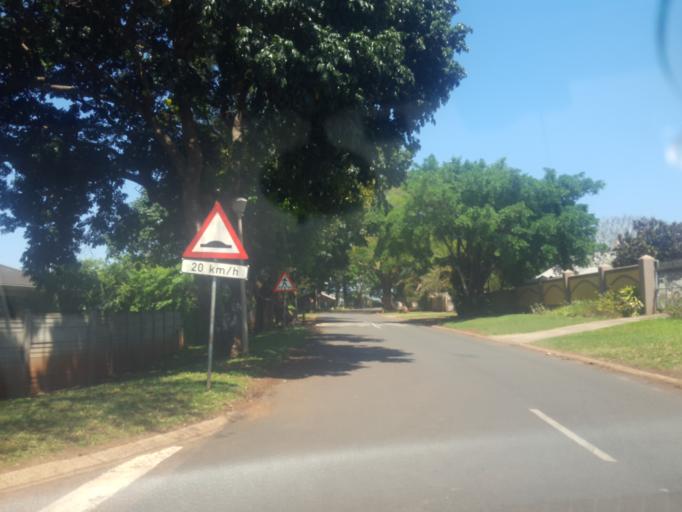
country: ZA
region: KwaZulu-Natal
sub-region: uThungulu District Municipality
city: Empangeni
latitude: -28.7493
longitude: 31.9053
